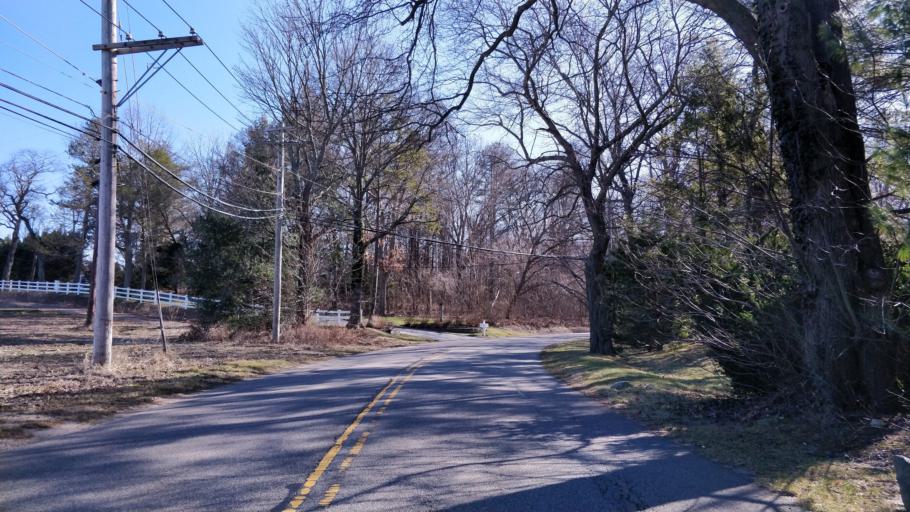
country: US
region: New York
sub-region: Nassau County
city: Glen Head
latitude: 40.8302
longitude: -73.6171
